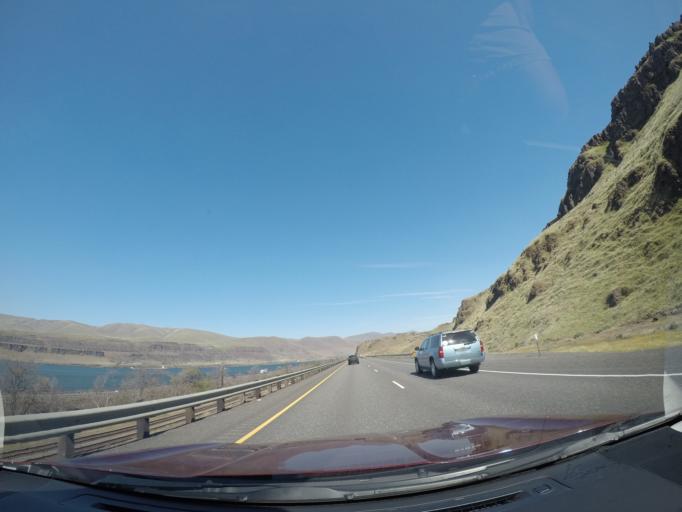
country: US
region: Washington
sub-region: Klickitat County
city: Dallesport
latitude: 45.6397
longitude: -121.0851
